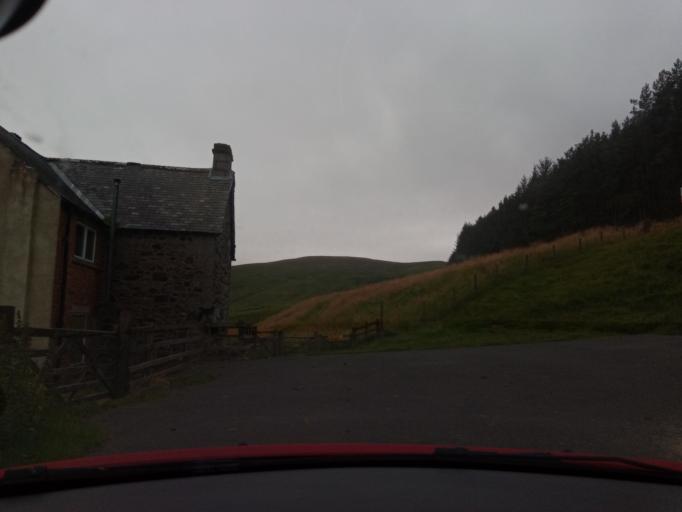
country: GB
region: England
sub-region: Northumberland
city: Rochester
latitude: 55.3951
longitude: -2.2447
